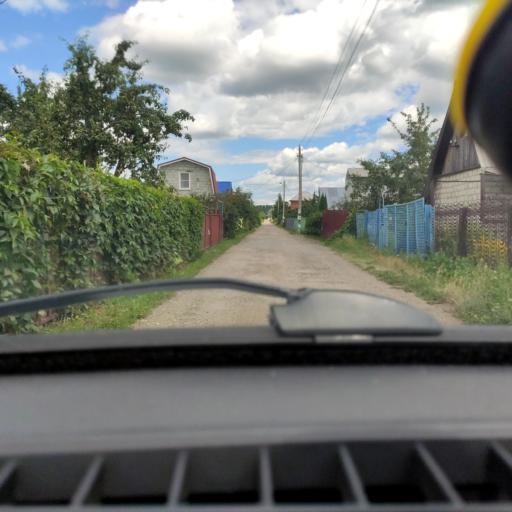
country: RU
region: Samara
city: Podstepki
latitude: 53.5991
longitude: 49.2248
